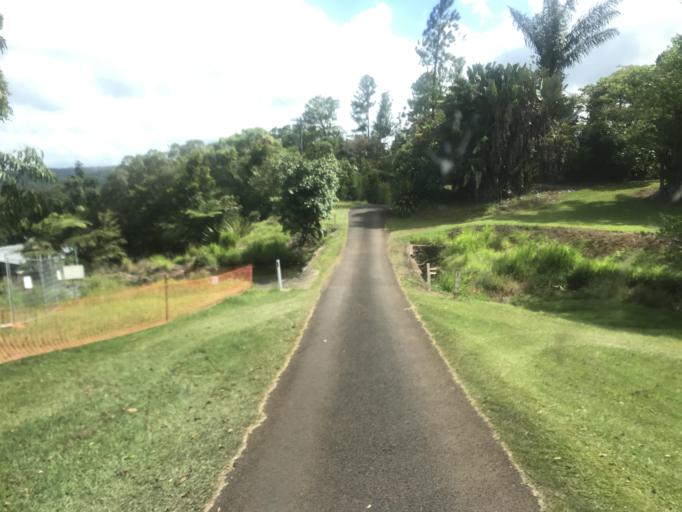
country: AU
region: Queensland
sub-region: Tablelands
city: Ravenshoe
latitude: -17.5503
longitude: 145.6977
